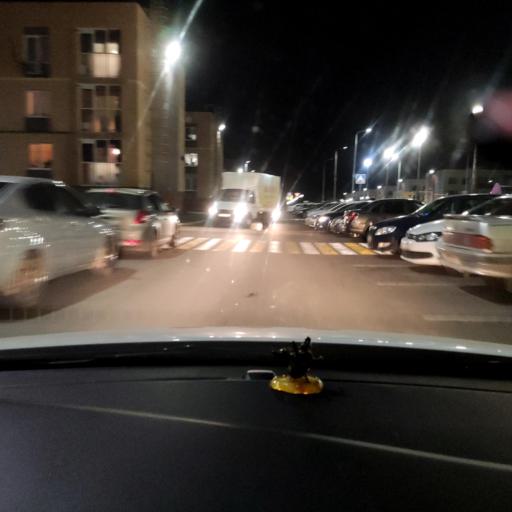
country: RU
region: Tatarstan
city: Vysokaya Gora
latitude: 55.8098
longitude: 49.4393
